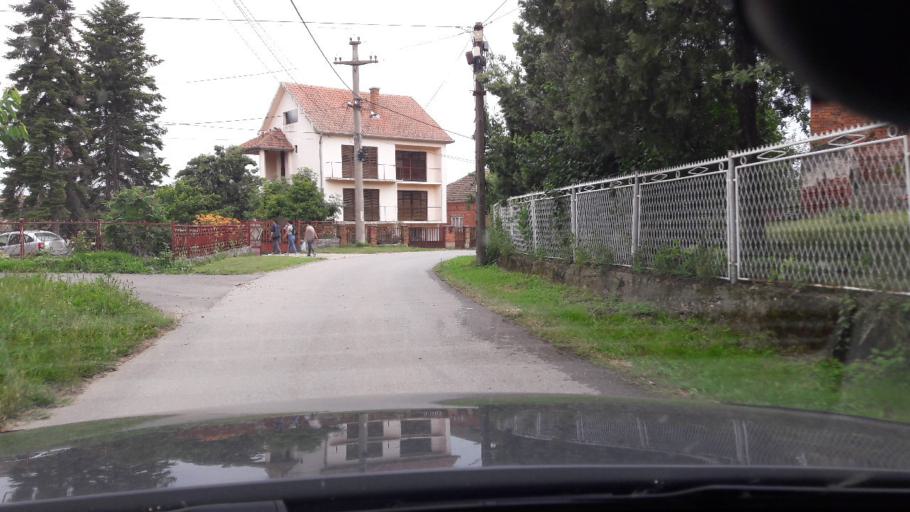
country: RS
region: Central Serbia
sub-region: Belgrade
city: Grocka
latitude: 44.6507
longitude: 20.6009
